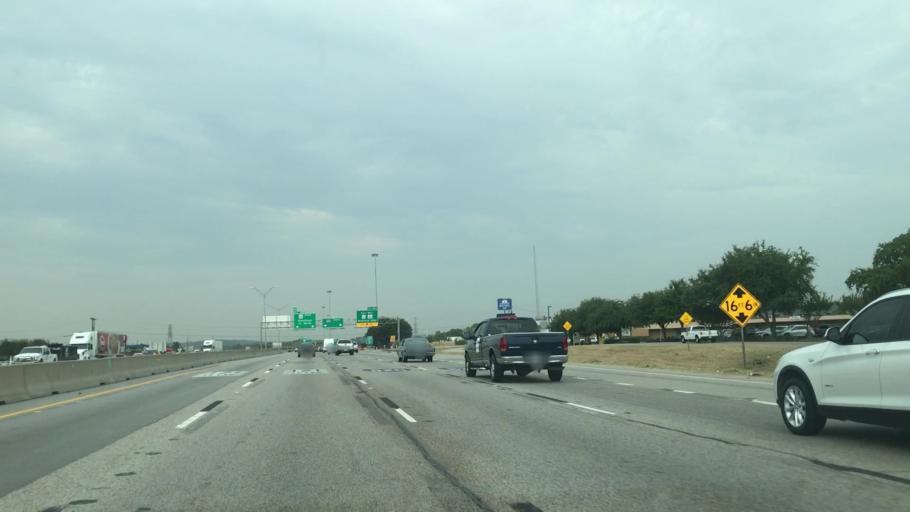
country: US
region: Texas
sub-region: Tarrant County
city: Richland Hills
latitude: 32.8136
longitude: -97.2079
